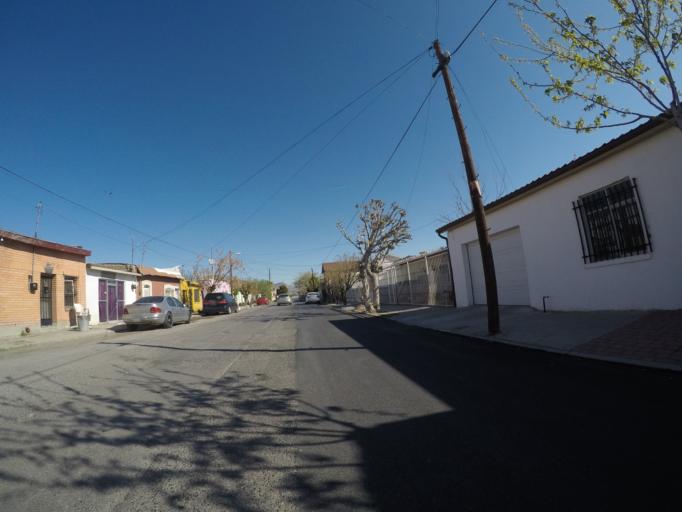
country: MX
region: Chihuahua
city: Ciudad Juarez
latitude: 31.7450
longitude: -106.4716
